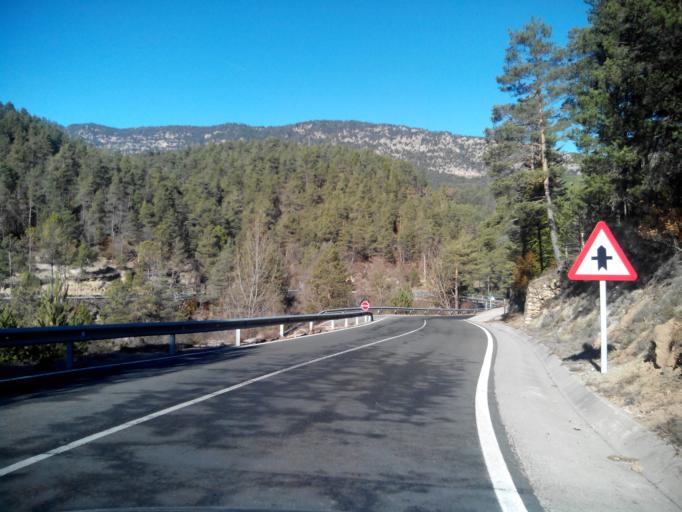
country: ES
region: Catalonia
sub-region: Provincia de Barcelona
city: Capolat
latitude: 42.1271
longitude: 1.6653
